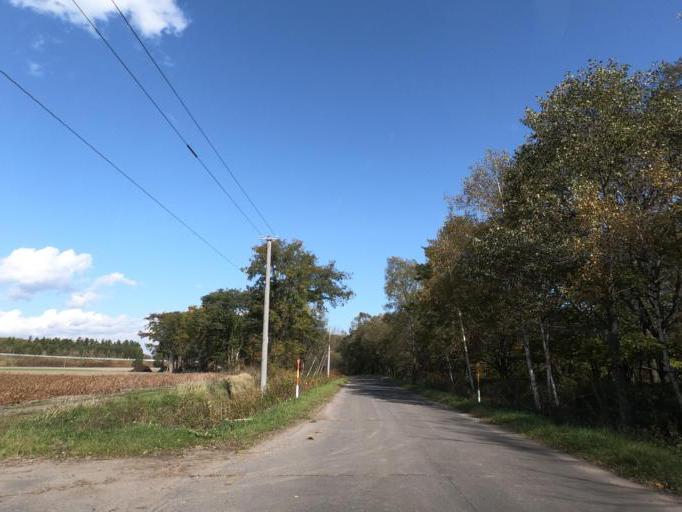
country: JP
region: Hokkaido
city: Otofuke
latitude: 43.2358
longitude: 143.2671
